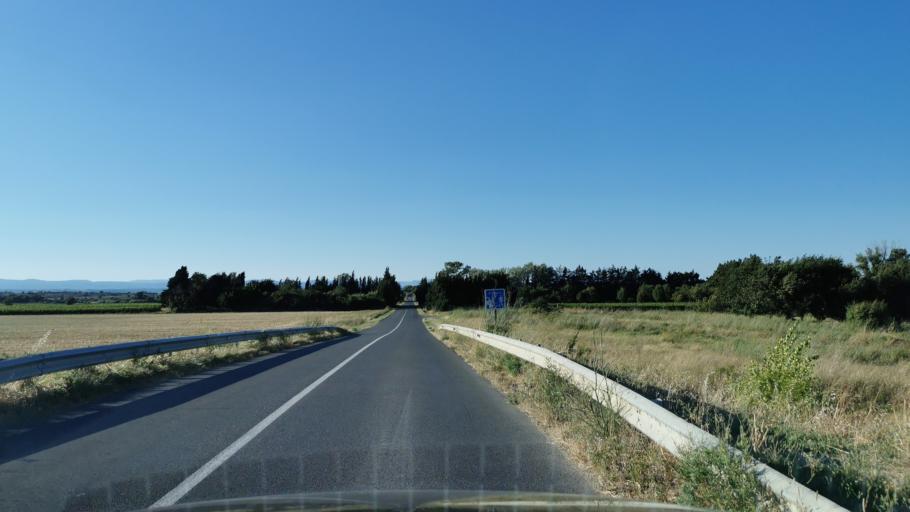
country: FR
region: Languedoc-Roussillon
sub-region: Departement de l'Aude
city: Ouveillan
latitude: 43.2541
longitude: 2.9965
